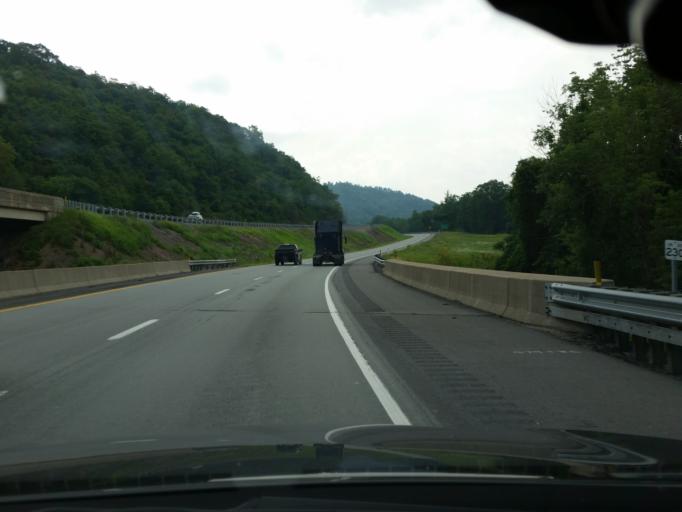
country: US
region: Pennsylvania
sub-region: Perry County
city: Newport
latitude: 40.4804
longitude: -77.0482
